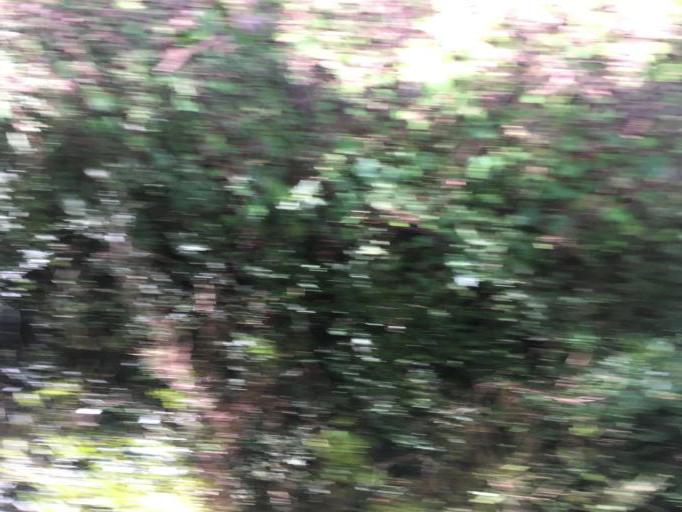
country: TW
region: Taiwan
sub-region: Yilan
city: Yilan
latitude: 24.7577
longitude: 121.6146
